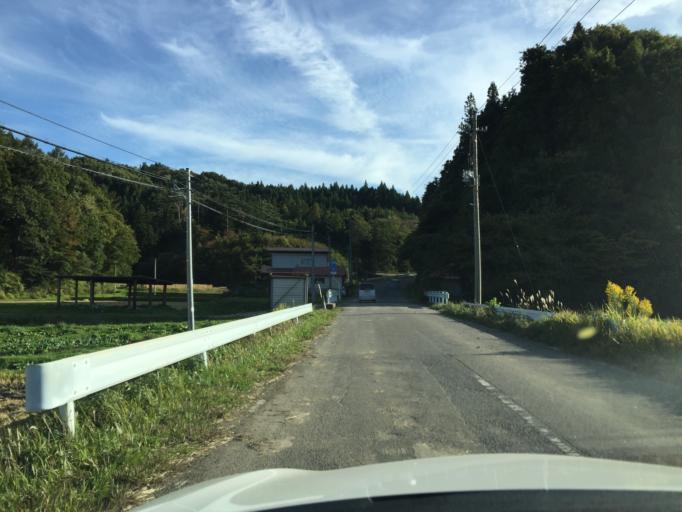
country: JP
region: Fukushima
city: Funehikimachi-funehiki
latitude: 37.2772
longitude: 140.6107
